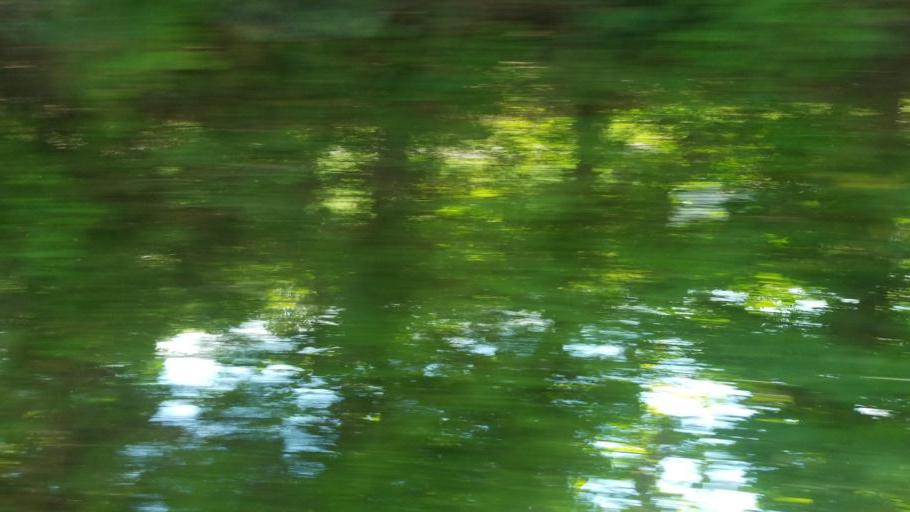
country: US
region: Illinois
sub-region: Williamson County
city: Johnston City
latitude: 37.7821
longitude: -88.8130
